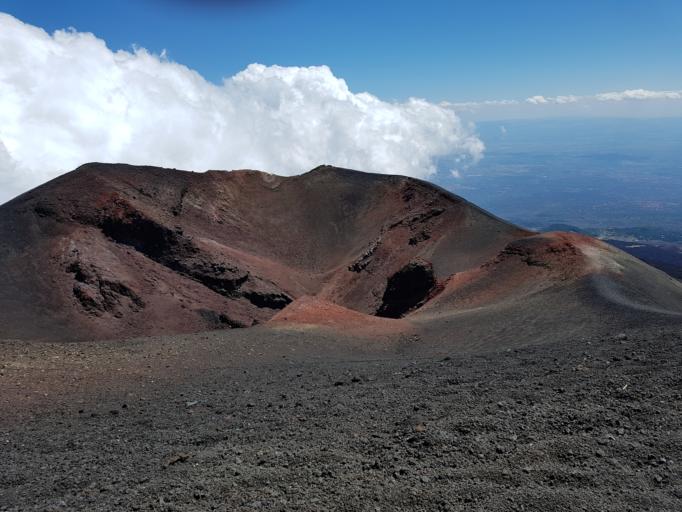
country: IT
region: Sicily
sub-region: Catania
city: Mineo
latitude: 37.2958
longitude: 14.6403
